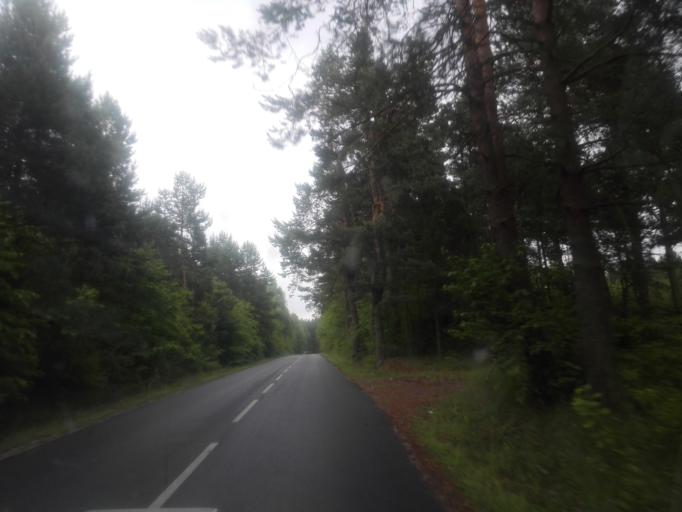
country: PL
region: Silesian Voivodeship
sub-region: Powiat myszkowski
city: Zarki
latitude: 50.7075
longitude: 19.3441
